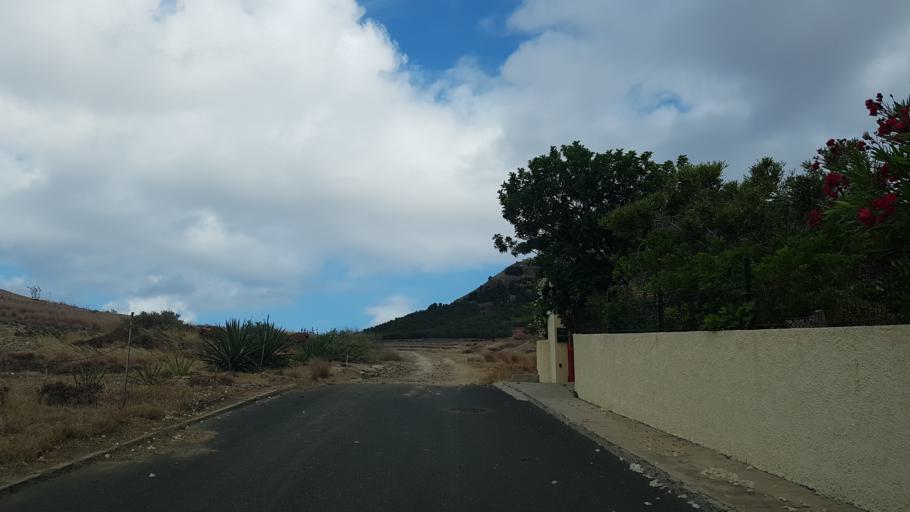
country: PT
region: Madeira
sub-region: Porto Santo
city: Vila de Porto Santo
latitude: 33.0403
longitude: -16.3625
